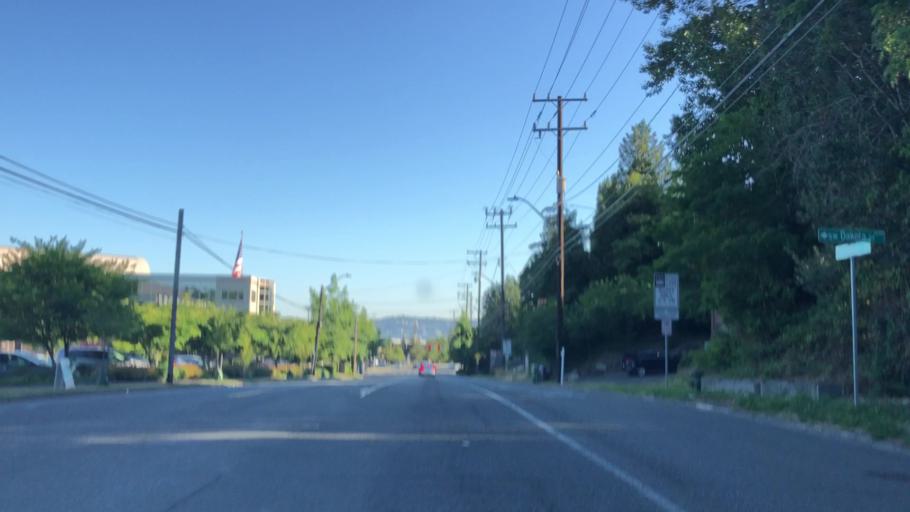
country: US
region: Washington
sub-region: King County
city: White Center
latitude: 47.5665
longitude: -122.3633
